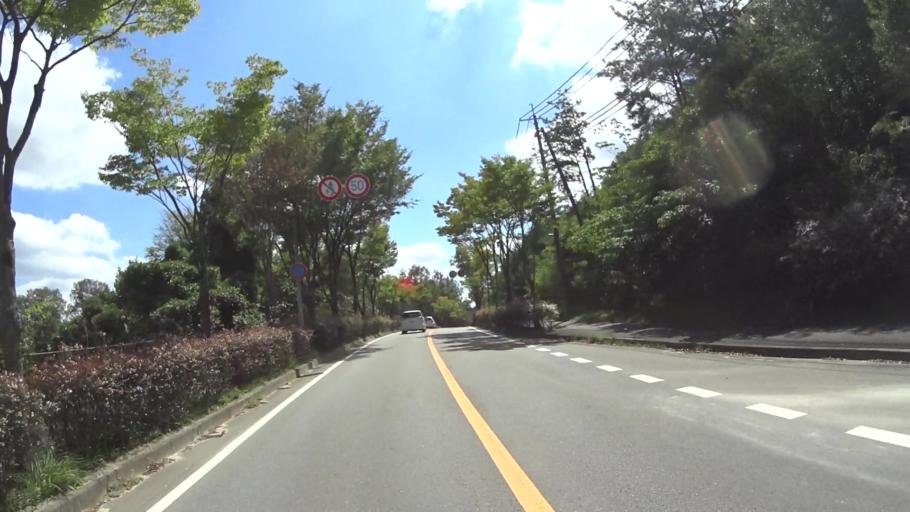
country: JP
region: Kyoto
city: Uji
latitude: 34.8596
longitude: 135.8001
